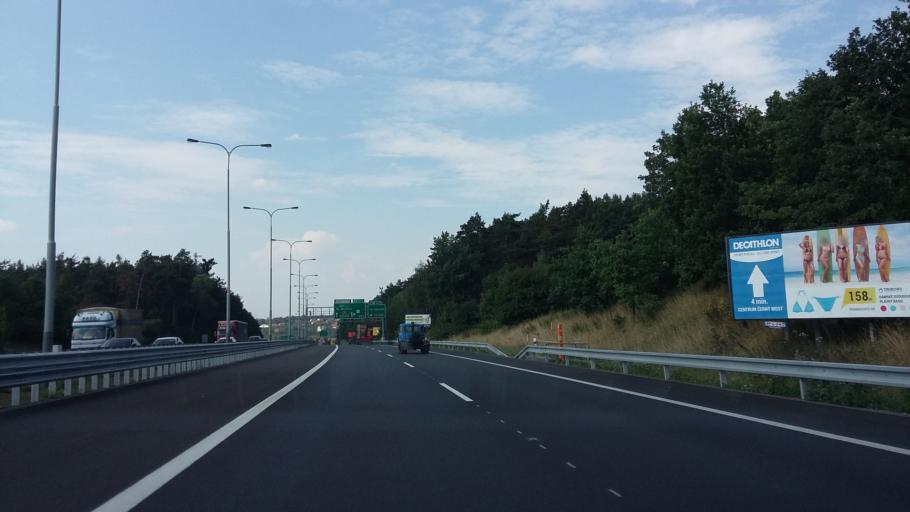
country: CZ
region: Praha
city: Cerny Most
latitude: 50.0904
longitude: 14.5950
